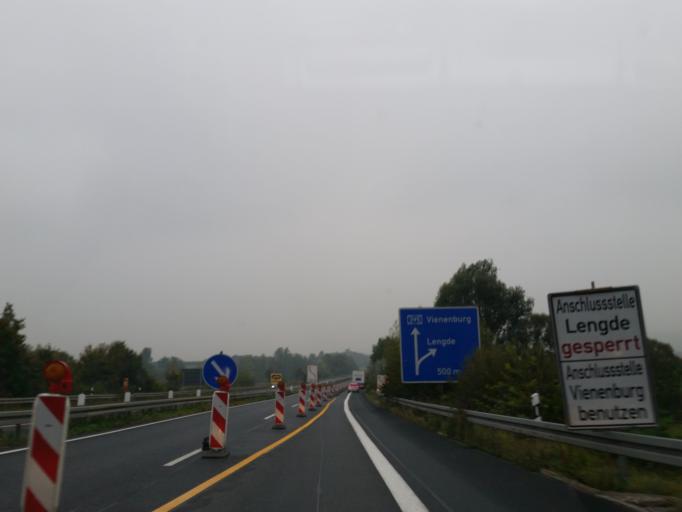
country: DE
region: Lower Saxony
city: Schladen
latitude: 51.9957
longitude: 10.5525
